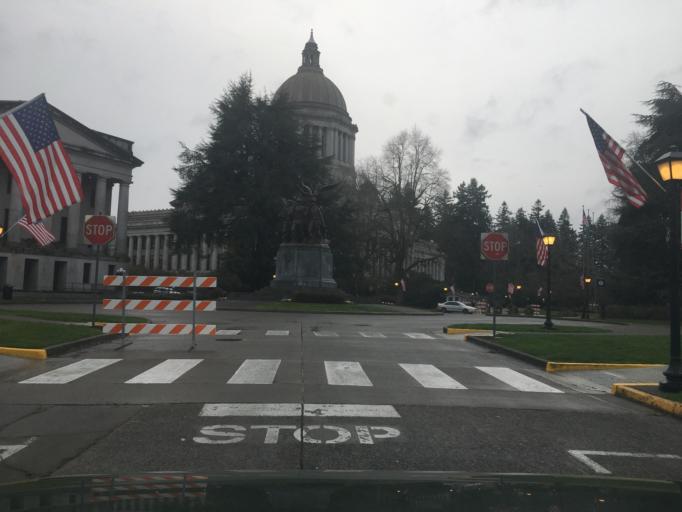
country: US
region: Washington
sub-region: Thurston County
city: Olympia
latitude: 47.0367
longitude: -122.9029
